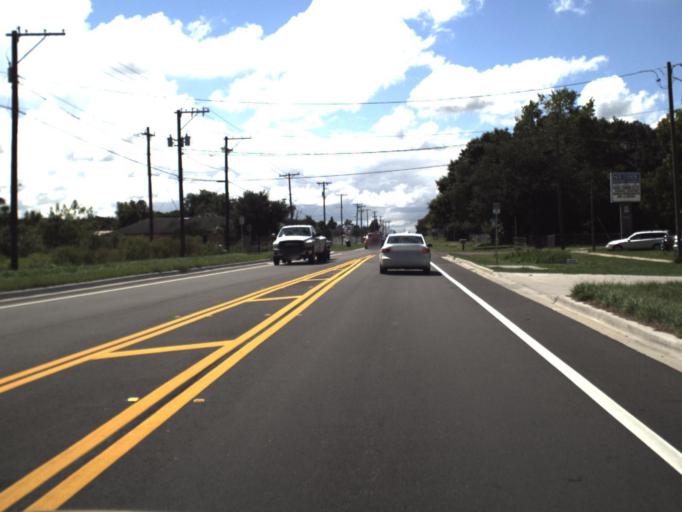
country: US
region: Florida
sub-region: Polk County
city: Mulberry
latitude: 27.8863
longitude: -81.9736
